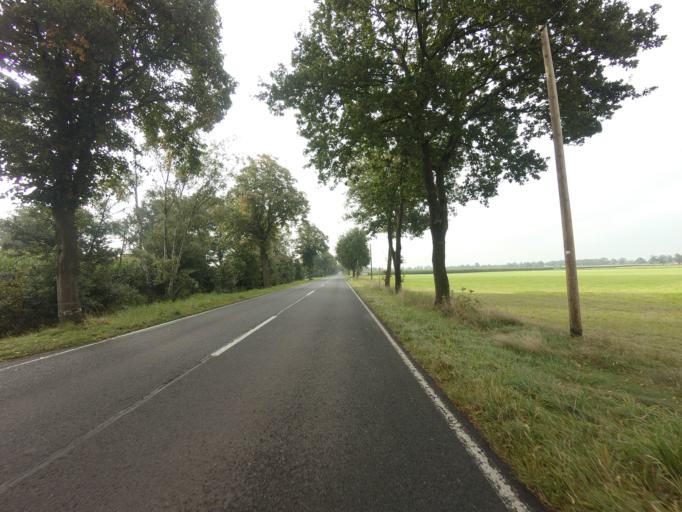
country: DE
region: Lower Saxony
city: Itterbeck
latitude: 52.4907
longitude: 6.7390
